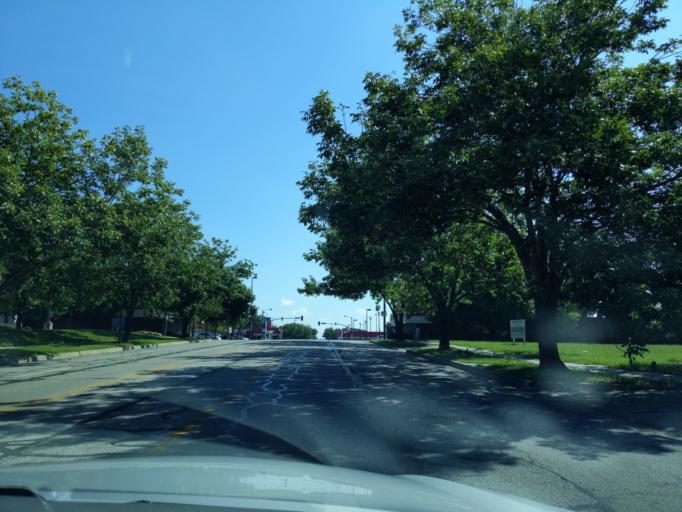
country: US
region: Missouri
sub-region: Jackson County
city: Kansas City
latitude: 39.0991
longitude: -94.5580
